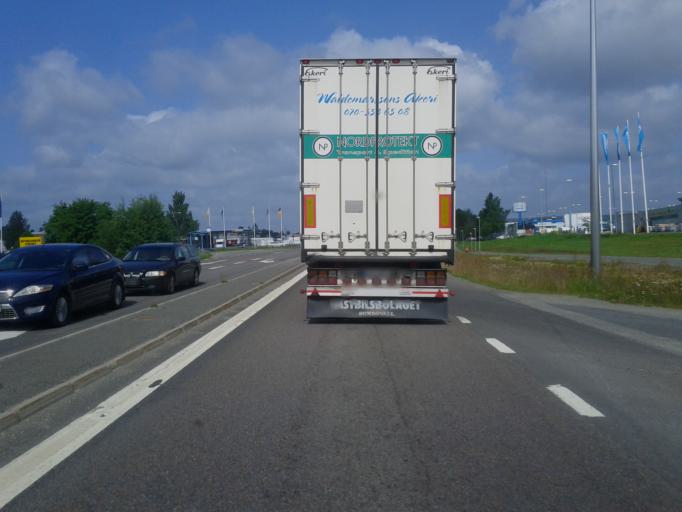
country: SE
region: Vaesterbotten
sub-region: Skelleftea Kommun
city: Skelleftea
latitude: 64.7356
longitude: 20.9677
